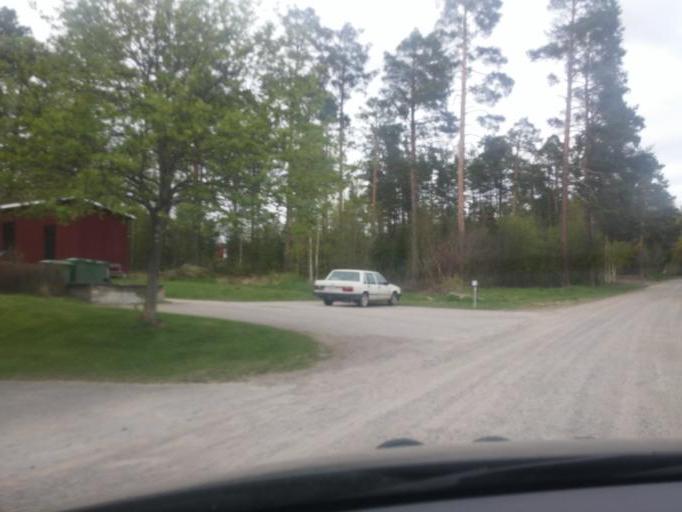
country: SE
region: Gaevleborg
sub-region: Ljusdals Kommun
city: Ljusdal
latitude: 61.8658
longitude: 16.0097
